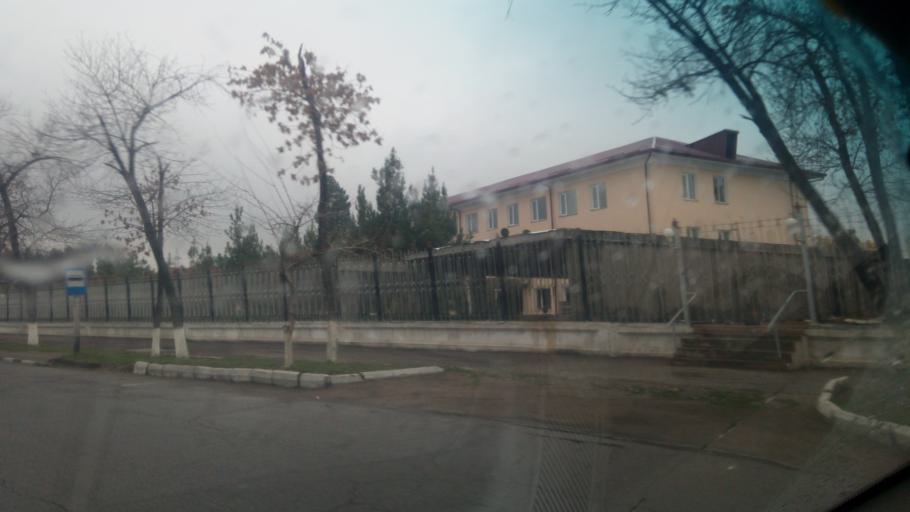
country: UZ
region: Toshkent Shahri
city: Bektemir
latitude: 41.2475
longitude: 69.3495
